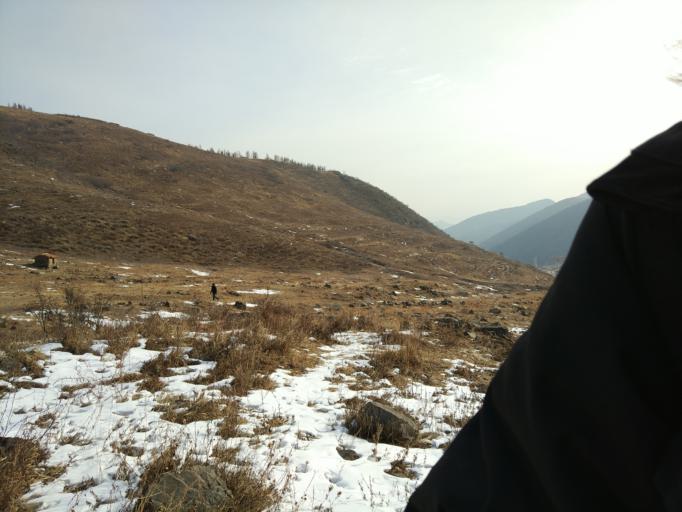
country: CN
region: Hebei
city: Xiwanzi
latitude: 40.8558
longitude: 115.4571
